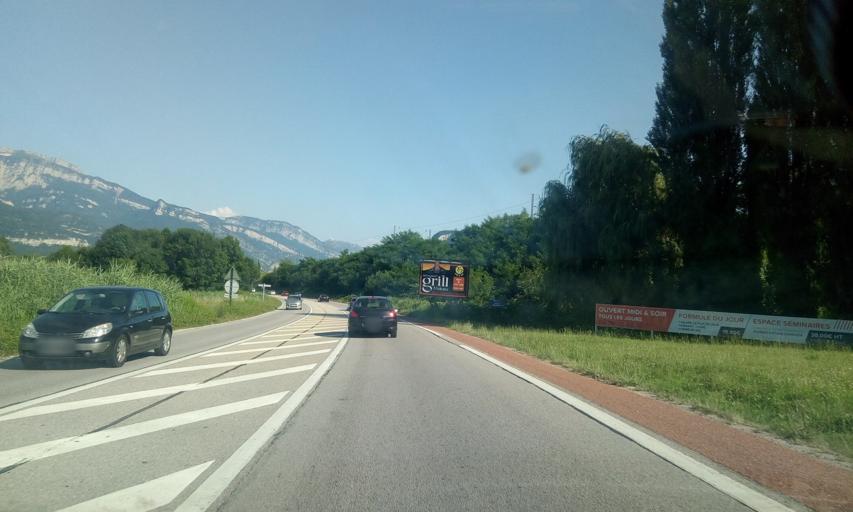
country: FR
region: Rhone-Alpes
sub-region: Departement de l'Isere
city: Moirans
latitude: 45.3286
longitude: 5.5700
